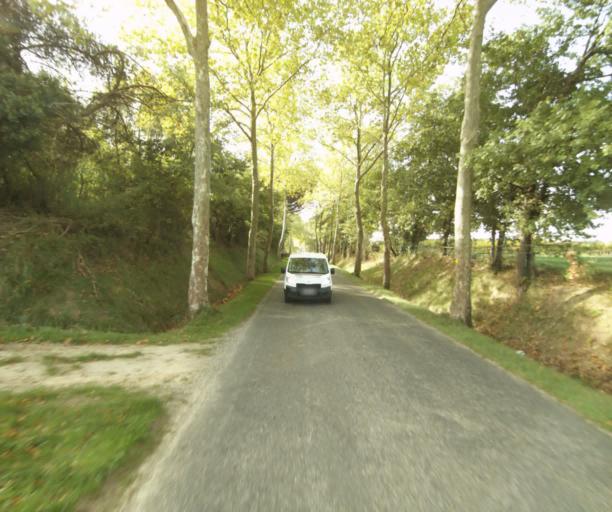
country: FR
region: Midi-Pyrenees
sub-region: Departement du Gers
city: Eauze
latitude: 43.9386
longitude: 0.0954
